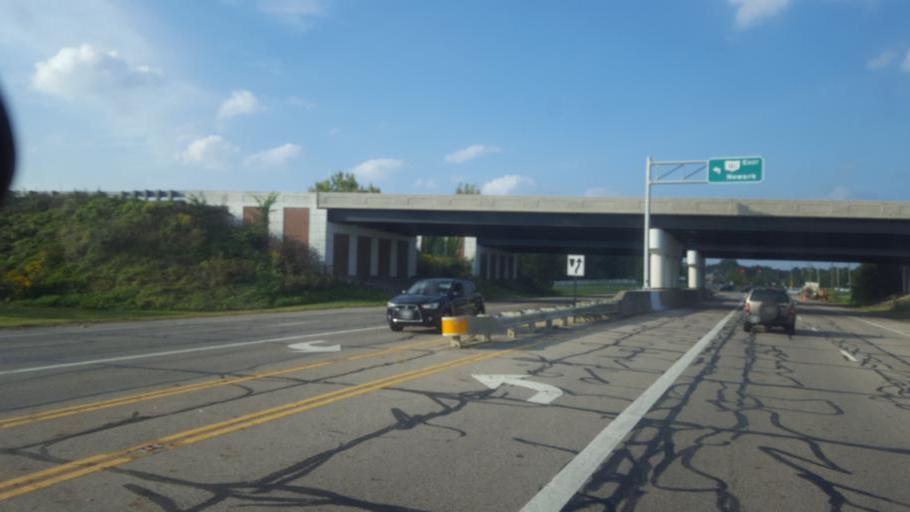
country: US
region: Ohio
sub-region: Franklin County
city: New Albany
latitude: 40.0885
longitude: -82.7977
